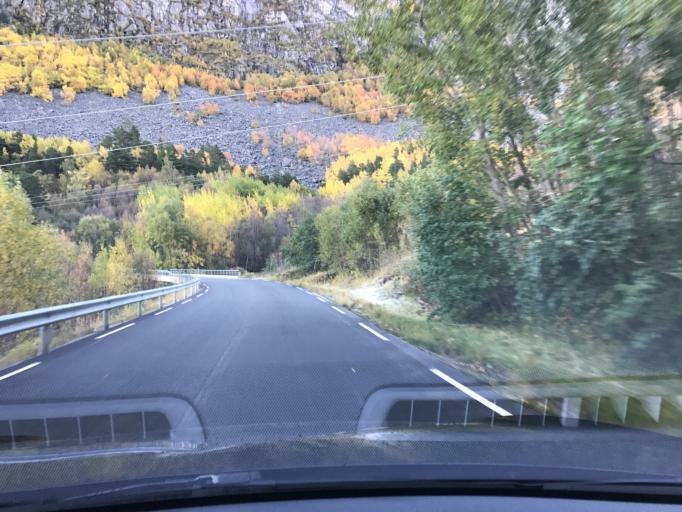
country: NO
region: Sogn og Fjordane
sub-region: Aurland
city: Aurlandsvangen
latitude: 60.8554
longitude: 7.3090
